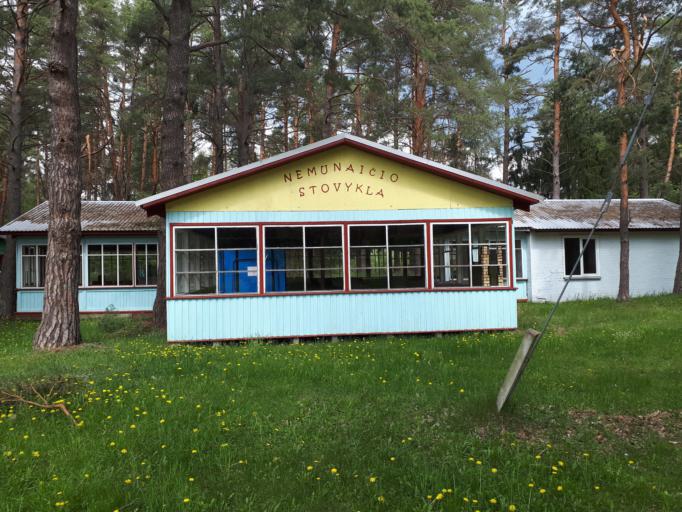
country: LT
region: Alytaus apskritis
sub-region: Alytus
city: Alytus
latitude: 54.3008
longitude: 24.0172
